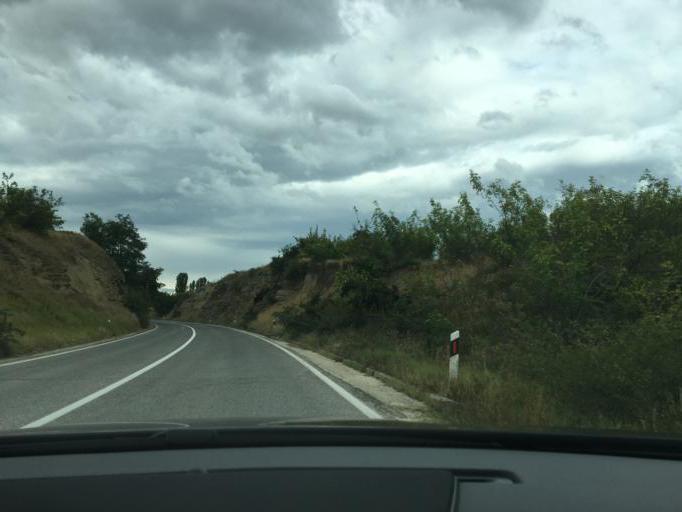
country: MK
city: Klechovce
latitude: 42.1546
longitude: 21.9513
